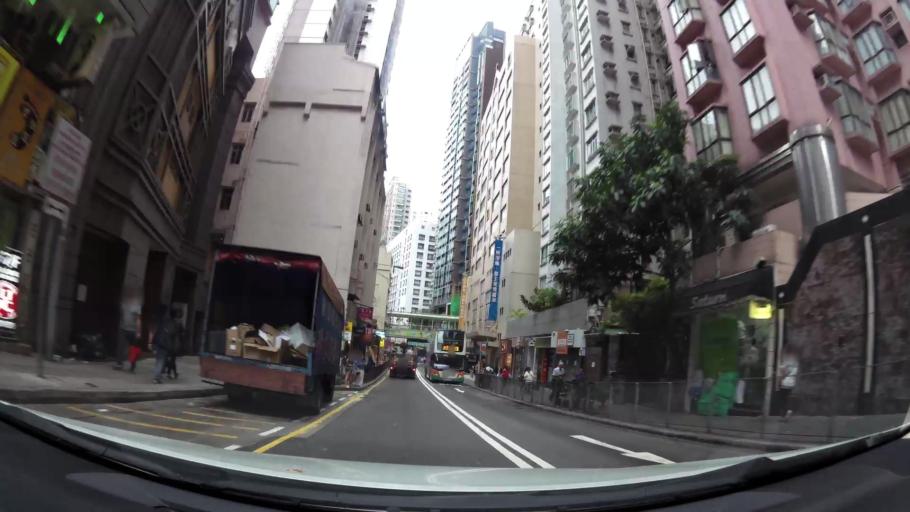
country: HK
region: Central and Western
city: Central
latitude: 22.2817
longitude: 114.1516
